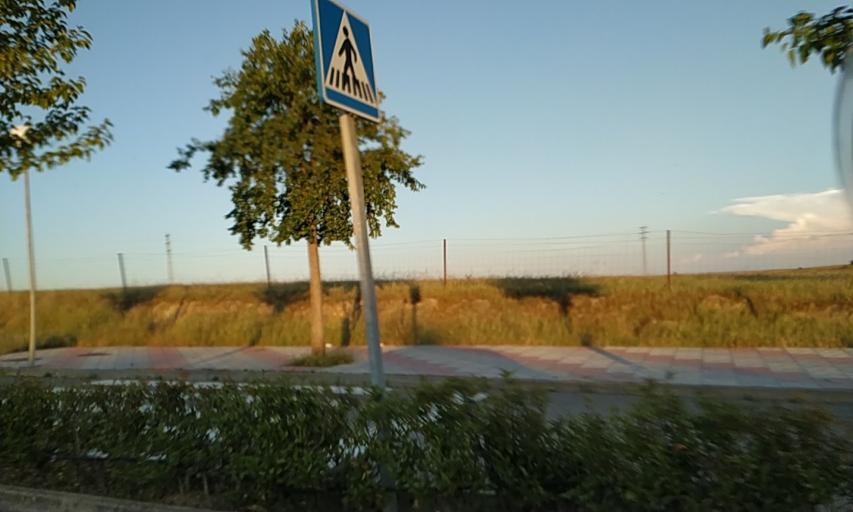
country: ES
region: Extremadura
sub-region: Provincia de Caceres
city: Salorino
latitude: 39.5291
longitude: -7.0503
